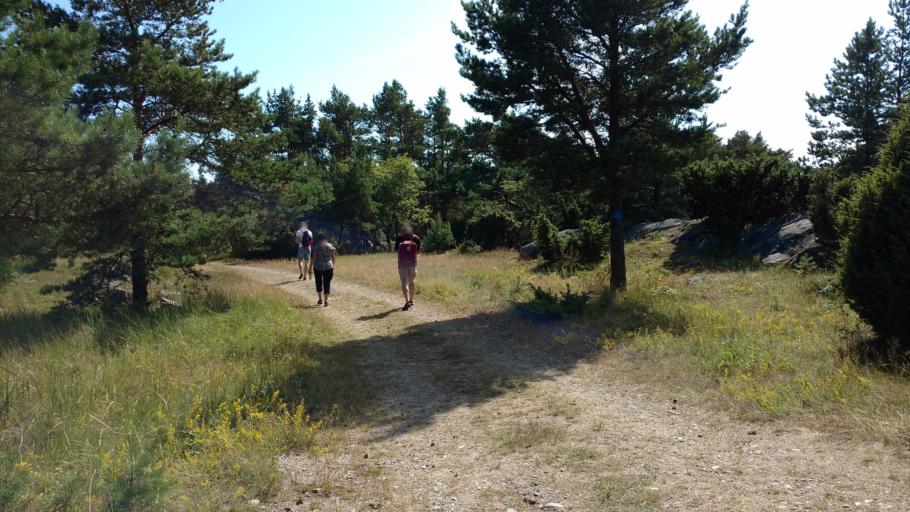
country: FI
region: Varsinais-Suomi
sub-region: Aboland-Turunmaa
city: Dragsfjaerd
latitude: 59.8079
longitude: 22.3149
